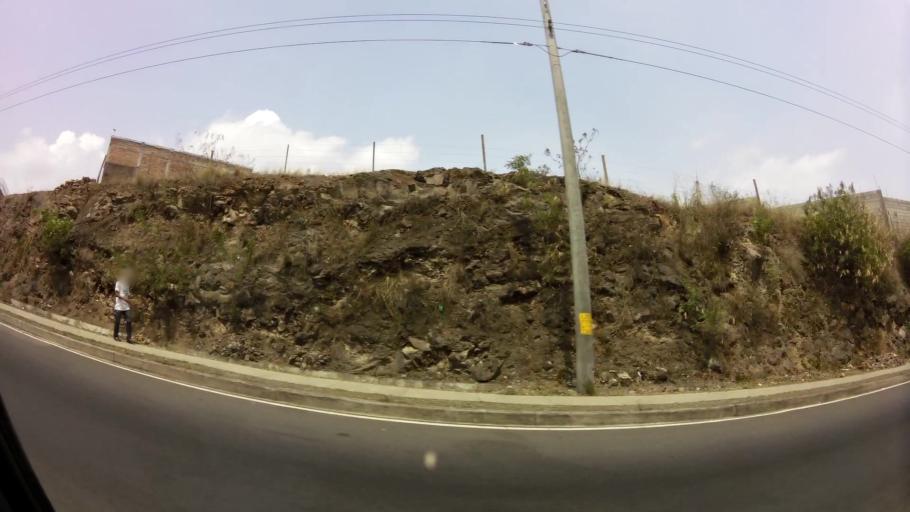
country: HN
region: Francisco Morazan
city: Tegucigalpa
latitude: 14.0769
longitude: -87.2362
